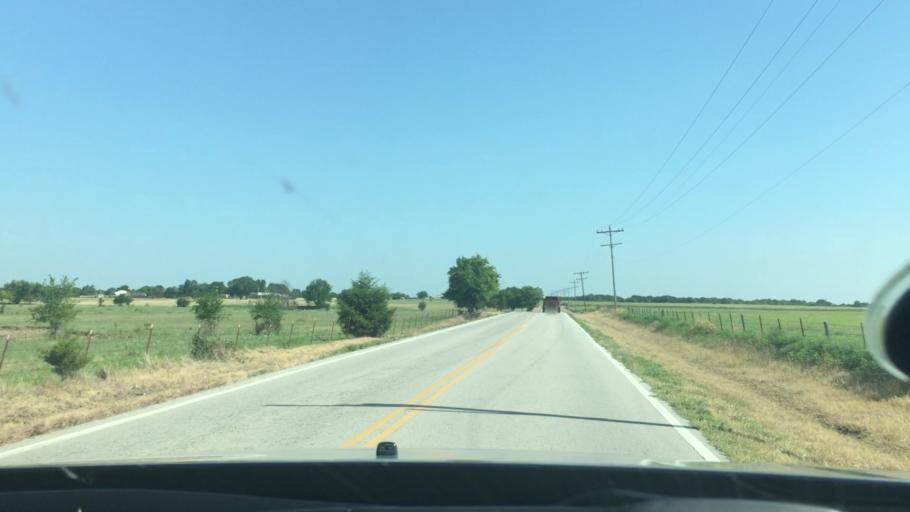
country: US
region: Oklahoma
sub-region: Bryan County
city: Durant
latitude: 34.1090
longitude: -96.4877
